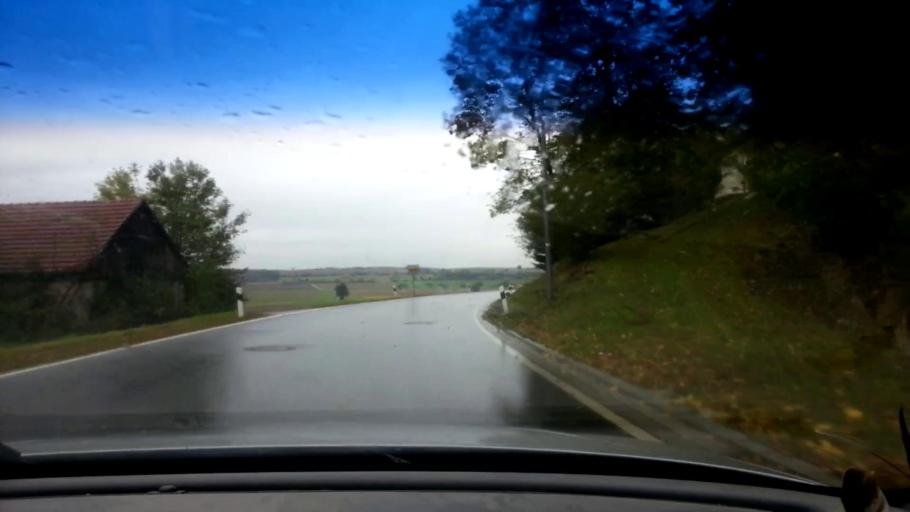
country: DE
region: Bavaria
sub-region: Upper Franconia
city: Konigsfeld
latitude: 49.9343
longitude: 11.1519
